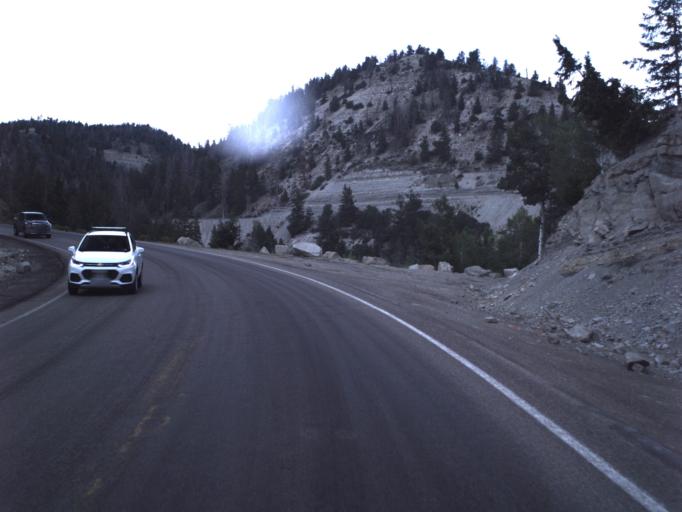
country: US
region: Utah
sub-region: Carbon County
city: Helper
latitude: 39.8632
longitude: -110.7652
